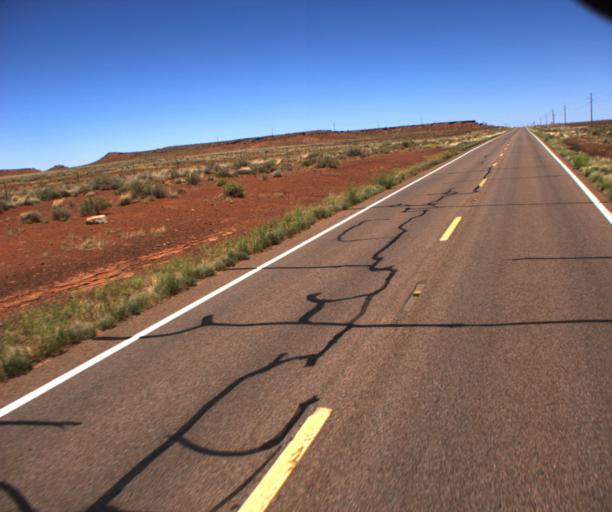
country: US
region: Arizona
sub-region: Coconino County
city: LeChee
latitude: 34.9262
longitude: -110.8071
